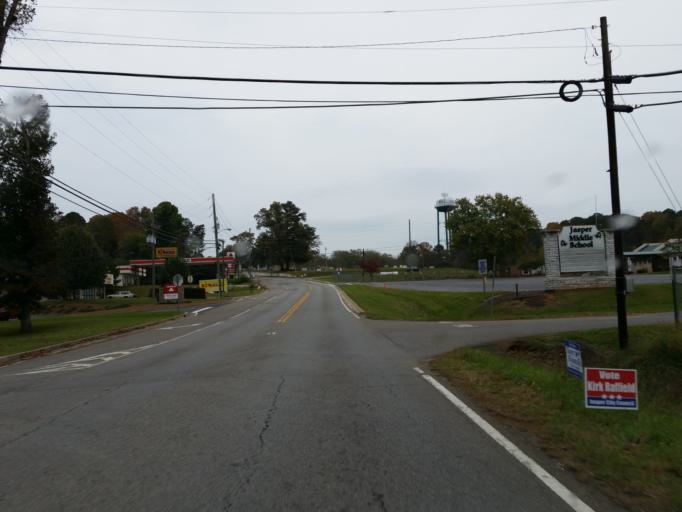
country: US
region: Georgia
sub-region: Pickens County
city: Jasper
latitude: 34.4659
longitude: -84.4365
